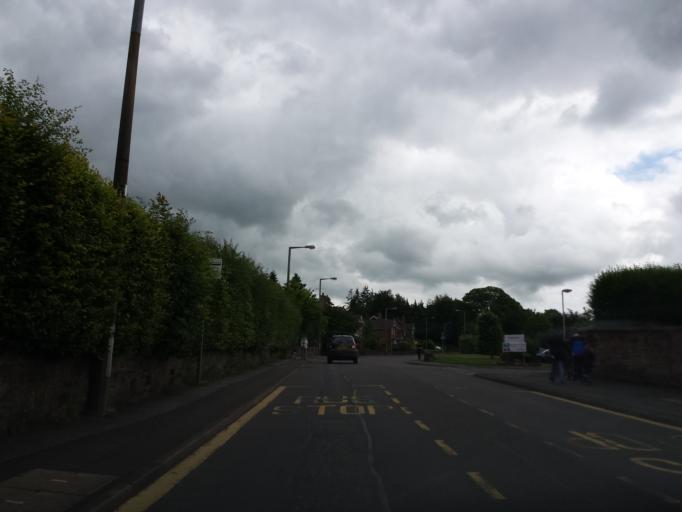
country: GB
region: Scotland
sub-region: Dumfries and Galloway
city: Dumfries
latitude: 55.0597
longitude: -3.6001
